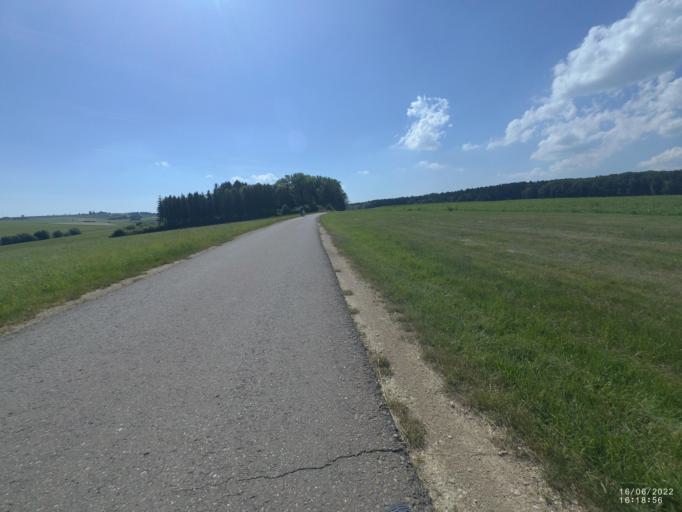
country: DE
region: Baden-Wuerttemberg
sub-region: Regierungsbezirk Stuttgart
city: Gerstetten
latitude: 48.6224
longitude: 10.0739
